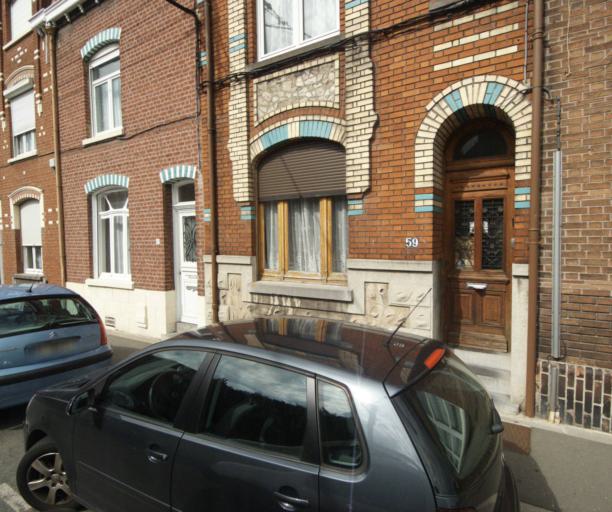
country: FR
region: Nord-Pas-de-Calais
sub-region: Departement du Nord
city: Marcq-en-Baroeul
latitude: 50.6586
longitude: 3.0763
